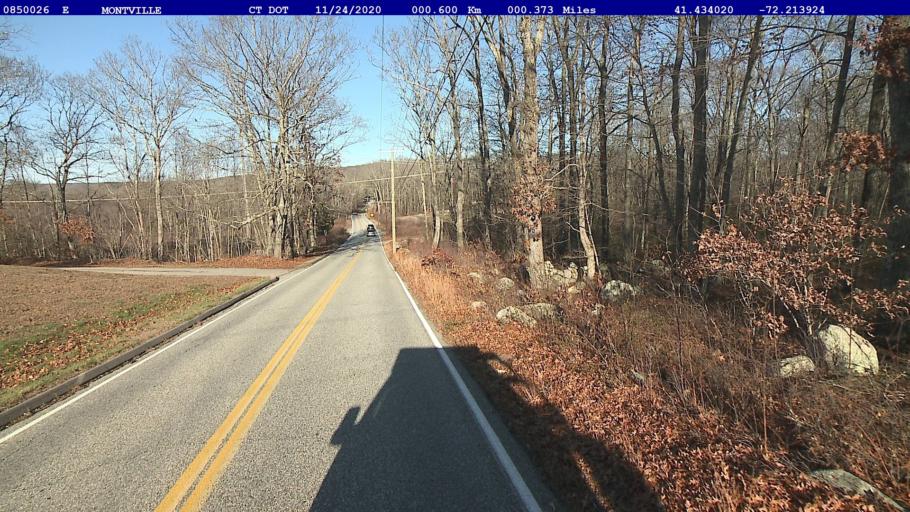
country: US
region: Connecticut
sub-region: New London County
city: Montville Center
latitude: 41.4340
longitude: -72.2139
